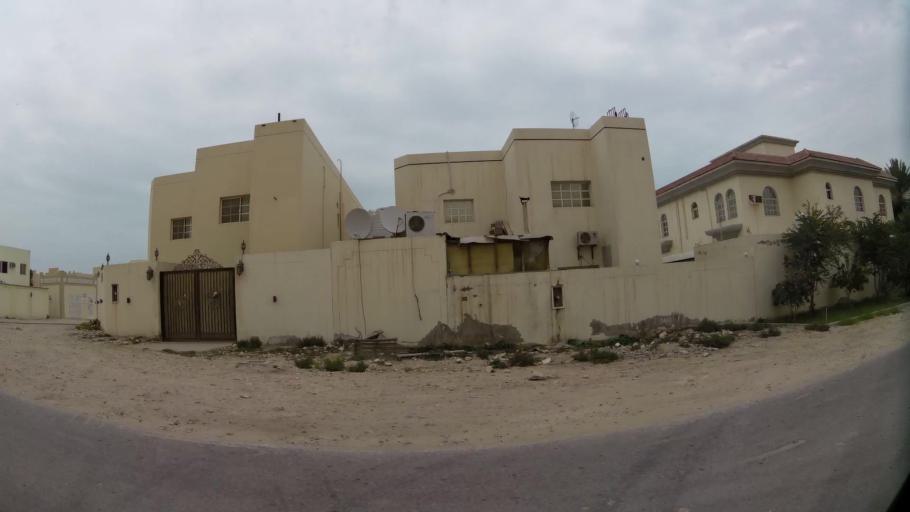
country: QA
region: Baladiyat ar Rayyan
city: Ar Rayyan
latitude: 25.3412
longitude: 51.4646
